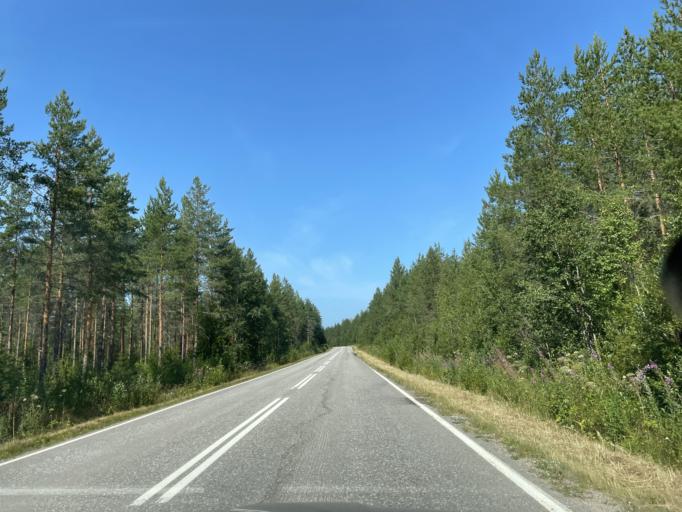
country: FI
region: Central Finland
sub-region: Saarijaervi-Viitasaari
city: Pihtipudas
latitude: 63.3634
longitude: 25.7179
